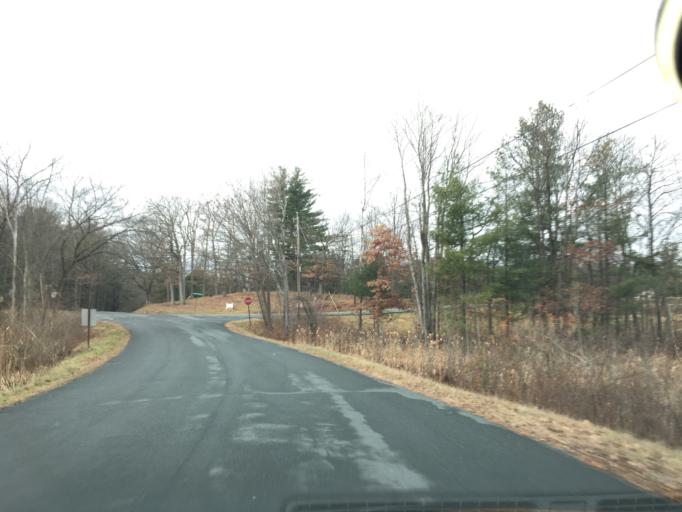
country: US
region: New York
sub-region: Rensselaer County
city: Averill Park
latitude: 42.6122
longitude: -73.5509
